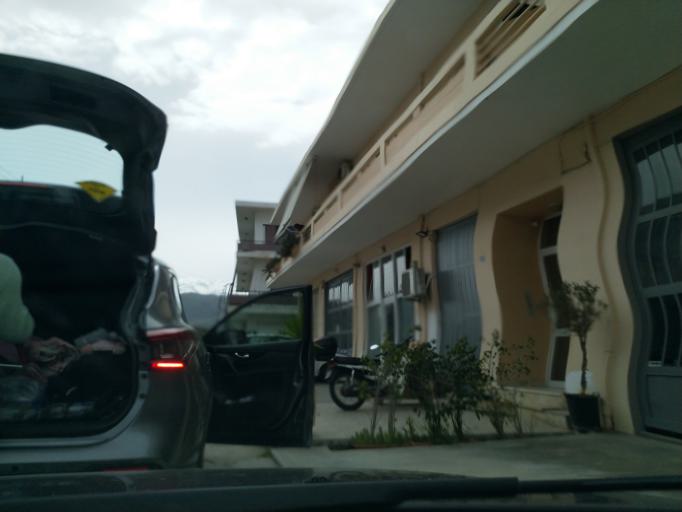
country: GR
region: Crete
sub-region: Nomos Chanias
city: Chania
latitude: 35.5018
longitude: 24.0230
